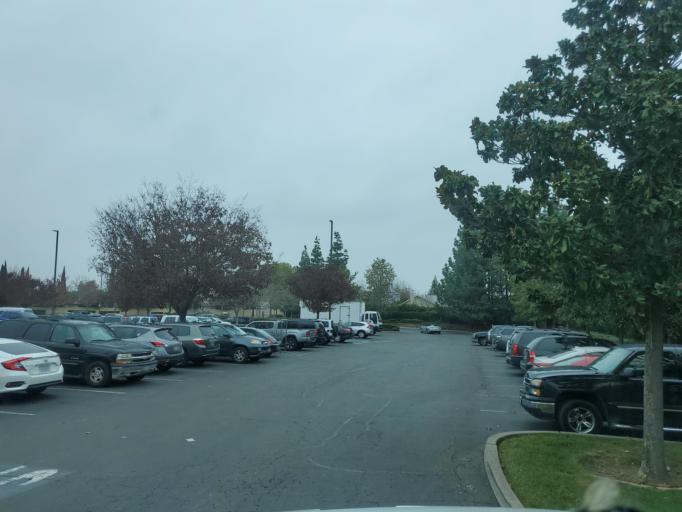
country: US
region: California
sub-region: San Joaquin County
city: August
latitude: 38.0053
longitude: -121.2833
